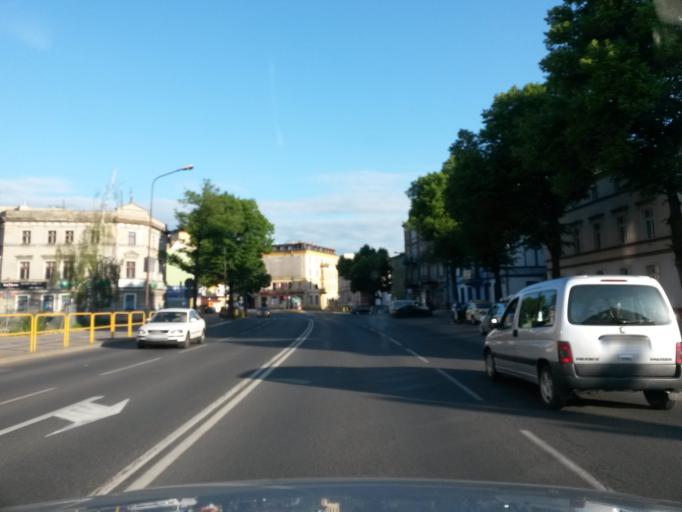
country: PL
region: Lower Silesian Voivodeship
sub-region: Jelenia Gora
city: Jelenia Gora
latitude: 50.9029
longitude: 15.7319
